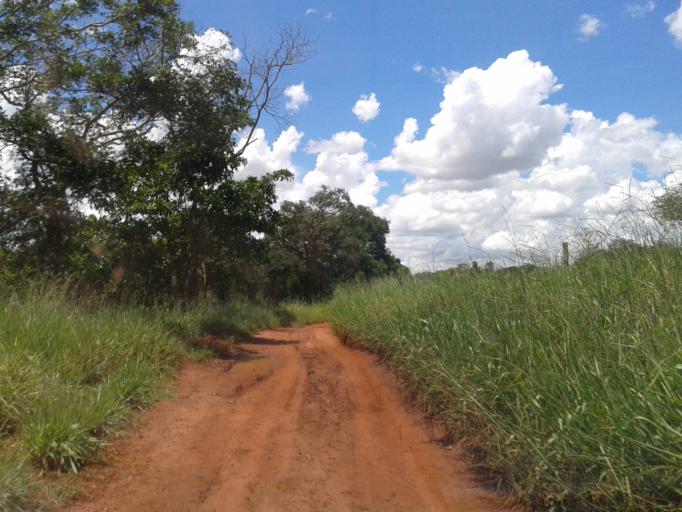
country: BR
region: Minas Gerais
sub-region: Santa Vitoria
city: Santa Vitoria
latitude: -18.7941
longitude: -49.8366
